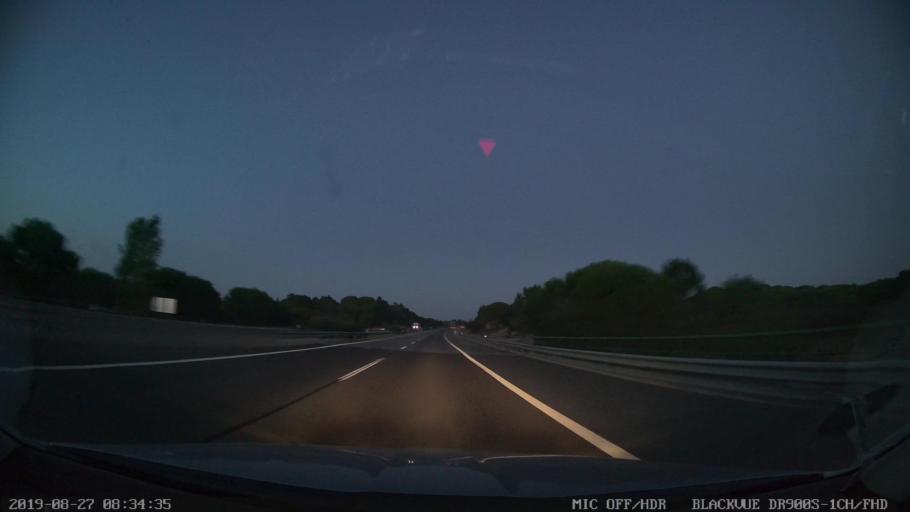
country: PT
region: Evora
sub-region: Vendas Novas
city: Vendas Novas
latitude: 38.6335
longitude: -8.5395
